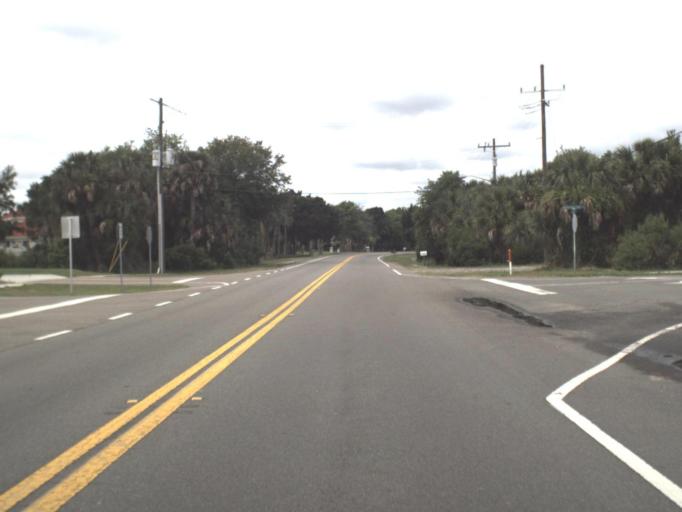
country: US
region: Florida
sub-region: Duval County
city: Atlantic Beach
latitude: 30.3912
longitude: -81.4403
